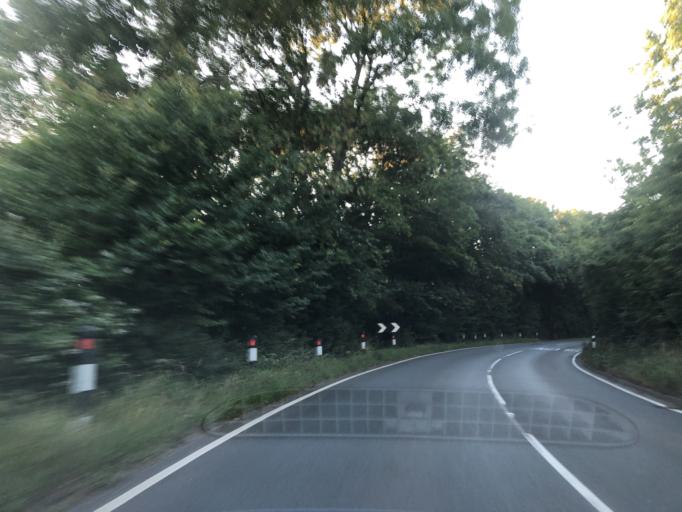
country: GB
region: England
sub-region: Isle of Wight
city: Newport
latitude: 50.6579
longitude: -1.2854
